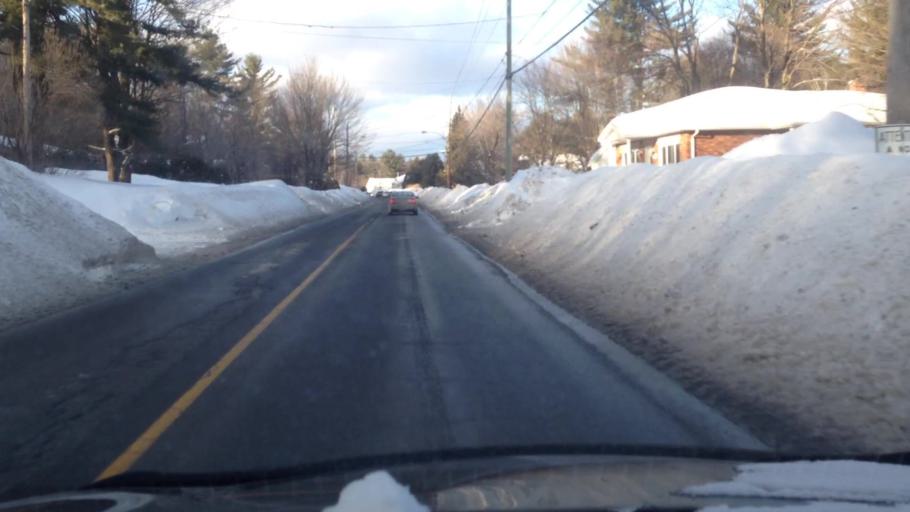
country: CA
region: Quebec
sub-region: Laurentides
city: Saint-Jerome
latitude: 45.8094
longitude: -73.9860
